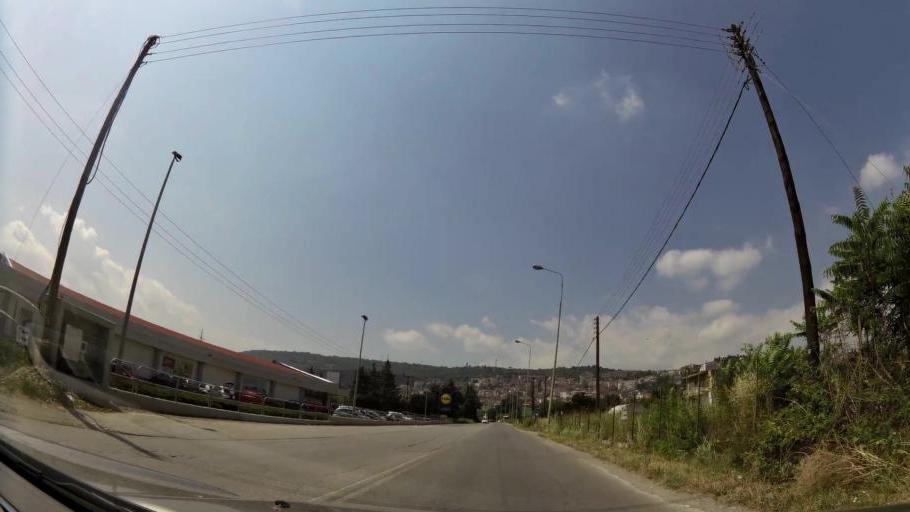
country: GR
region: Central Macedonia
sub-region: Nomos Imathias
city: Veroia
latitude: 40.5207
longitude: 22.2133
